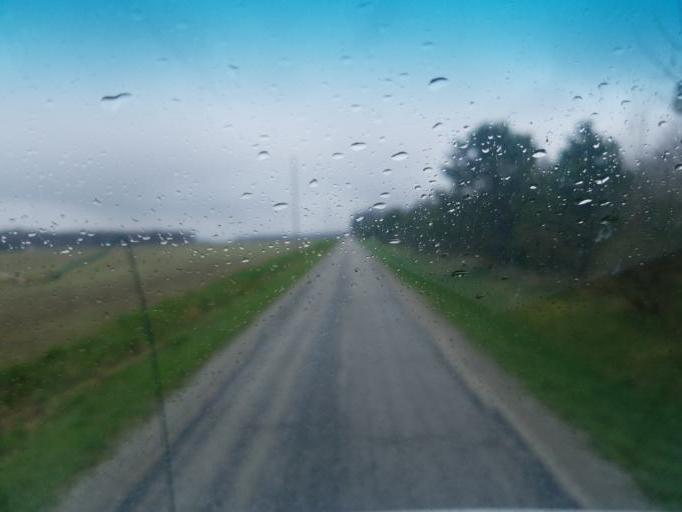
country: US
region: Ohio
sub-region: Crawford County
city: Bucyrus
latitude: 40.9221
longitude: -82.9973
